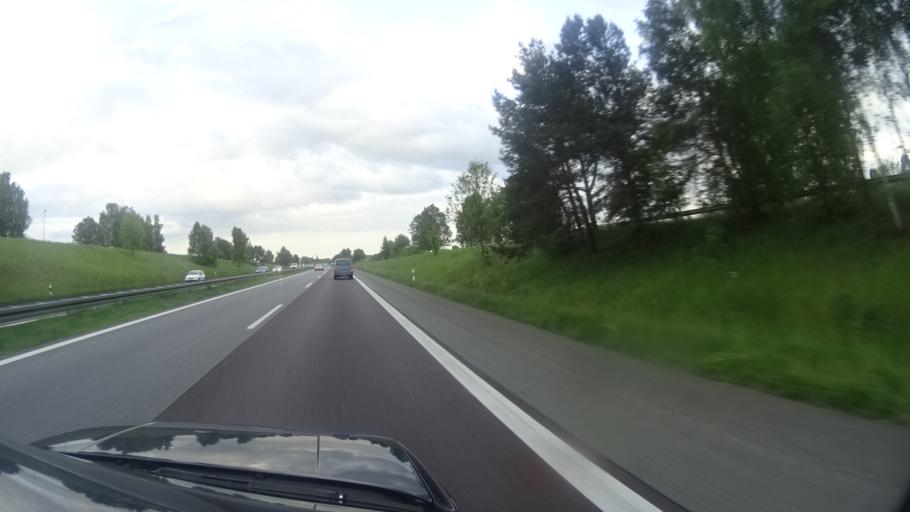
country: DE
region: Brandenburg
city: Walsleben
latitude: 52.9499
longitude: 12.6618
